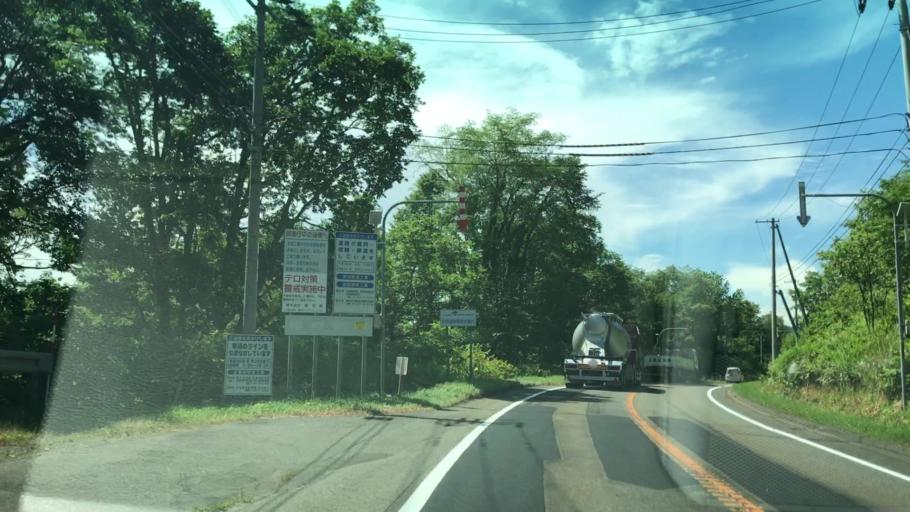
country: JP
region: Hokkaido
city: Shimo-furano
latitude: 42.9121
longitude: 142.4468
